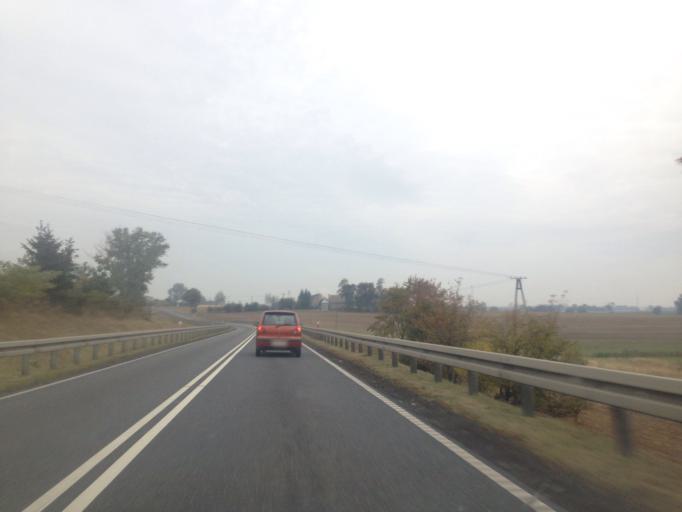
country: PL
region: Kujawsko-Pomorskie
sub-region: Powiat mogilenski
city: Mogilno
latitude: 52.6216
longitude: 17.9786
